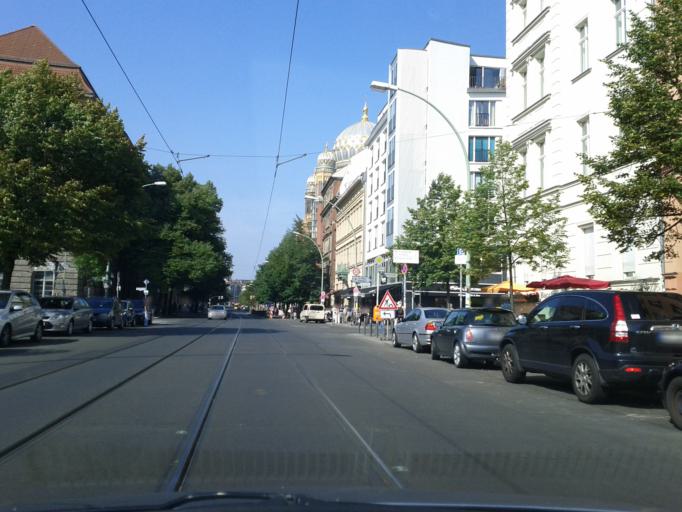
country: DE
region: Berlin
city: Mitte
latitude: 52.5242
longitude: 13.3959
